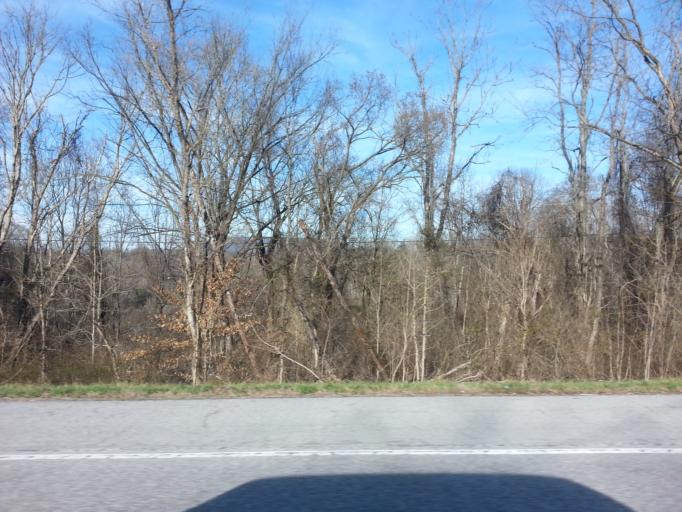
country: US
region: Tennessee
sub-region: Cannon County
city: Woodbury
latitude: 35.8072
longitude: -86.0258
